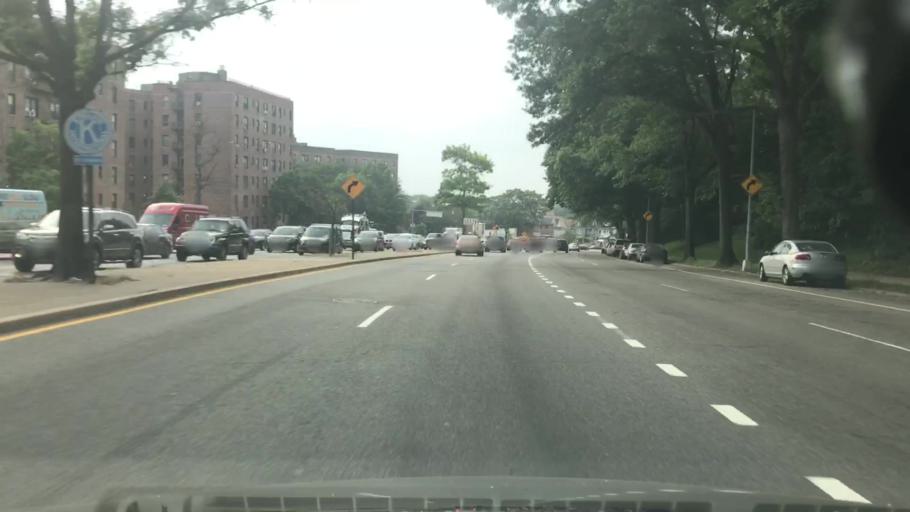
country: US
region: New York
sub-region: Queens County
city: Borough of Queens
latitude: 40.7001
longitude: -73.8542
